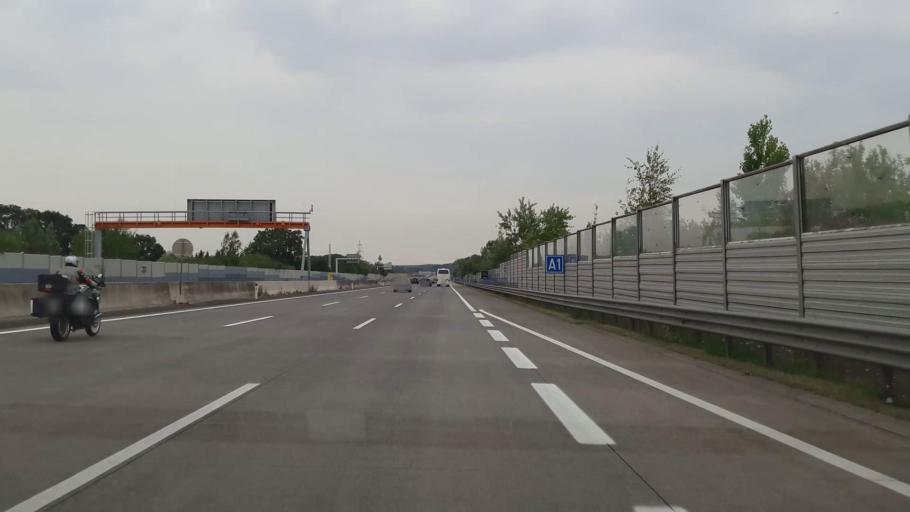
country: AT
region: Upper Austria
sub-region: Wels-Land
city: Sattledt
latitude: 48.0771
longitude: 14.0539
